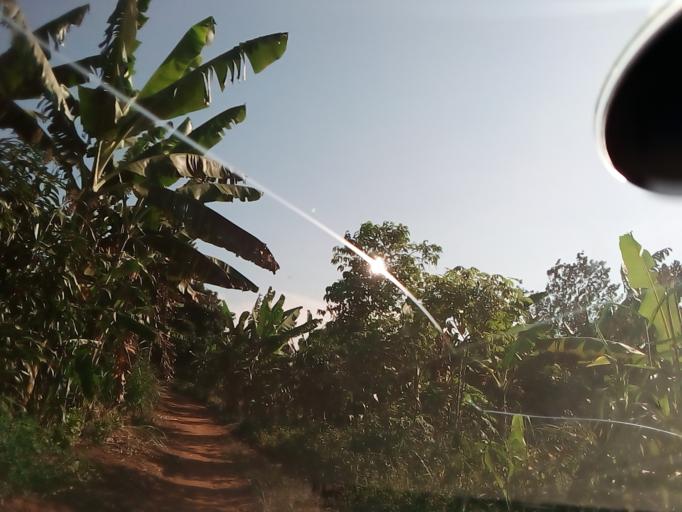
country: UG
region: Central Region
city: Masaka
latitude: -0.2701
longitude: 31.7202
